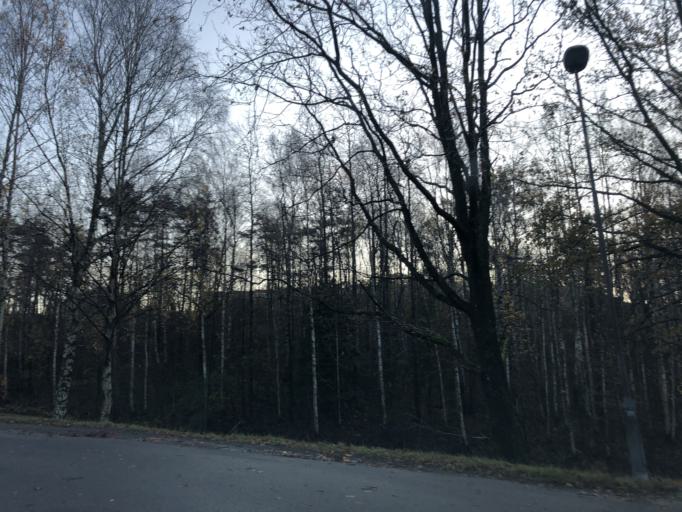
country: SE
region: Vaestra Goetaland
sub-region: Goteborg
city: Hammarkullen
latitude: 57.7809
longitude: 12.0255
